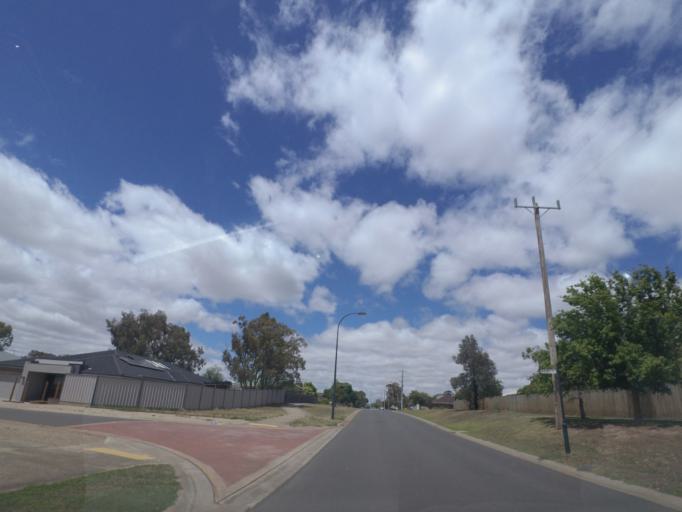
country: AU
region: Victoria
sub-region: Moorabool
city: Bacchus Marsh
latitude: -37.6522
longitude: 144.4434
